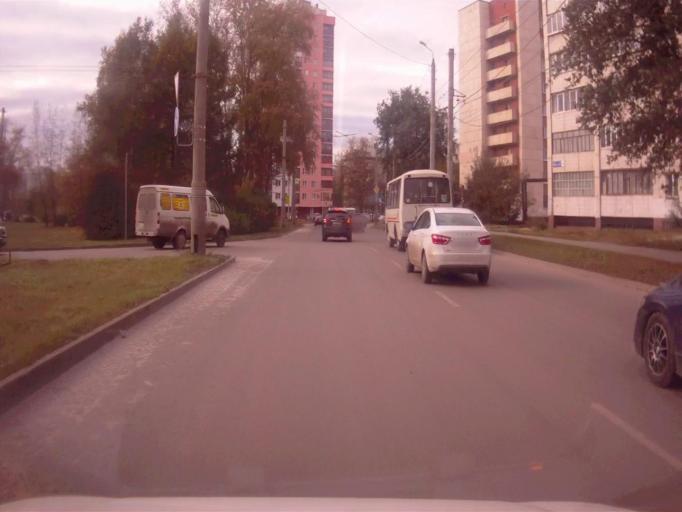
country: RU
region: Chelyabinsk
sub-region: Gorod Chelyabinsk
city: Chelyabinsk
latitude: 55.1168
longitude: 61.4382
